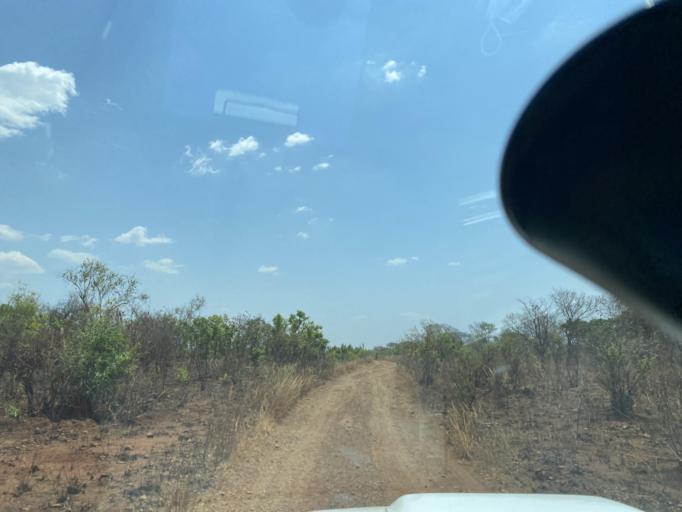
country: ZM
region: Lusaka
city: Lusaka
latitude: -15.5085
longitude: 27.9888
